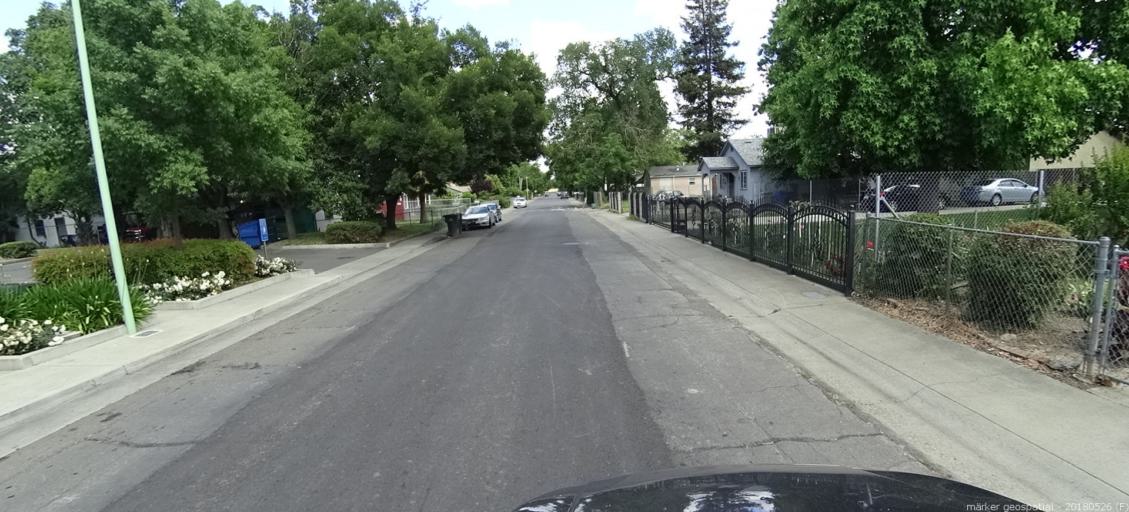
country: US
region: California
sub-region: Sacramento County
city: Sacramento
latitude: 38.6103
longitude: -121.4742
